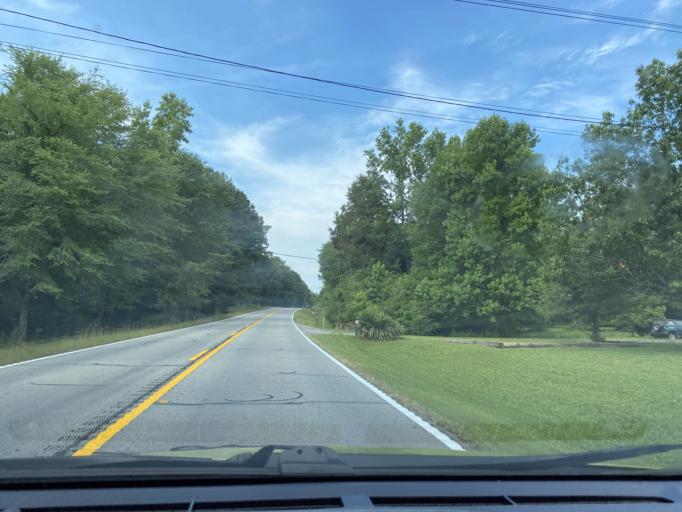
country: US
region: Georgia
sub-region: Coweta County
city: East Newnan
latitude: 33.2928
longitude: -84.6904
